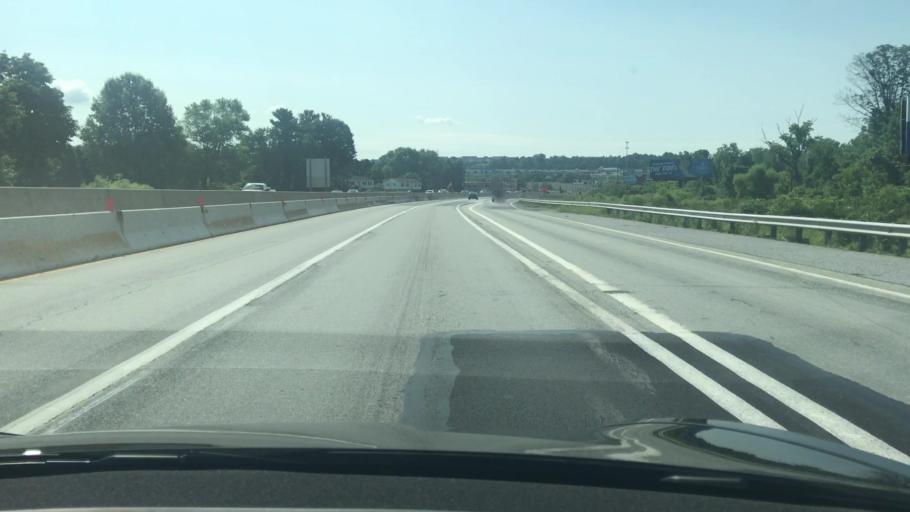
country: US
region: Pennsylvania
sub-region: York County
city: East York
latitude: 39.9653
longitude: -76.6878
